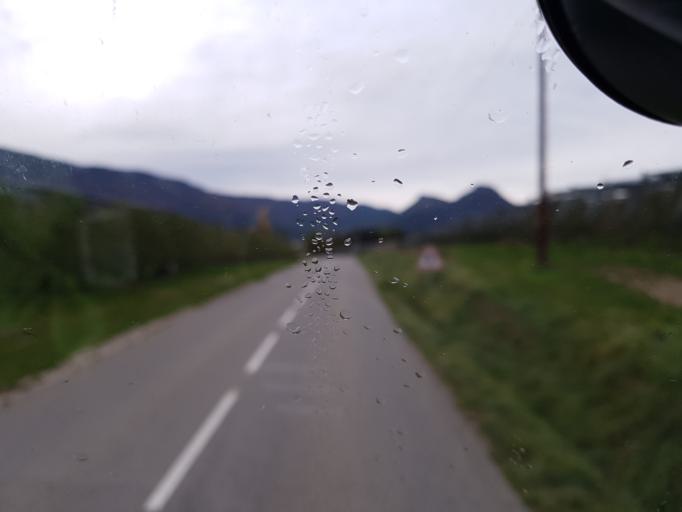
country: FR
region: Provence-Alpes-Cote d'Azur
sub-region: Departement des Hautes-Alpes
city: Laragne-Monteglin
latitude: 44.3290
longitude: 5.7469
